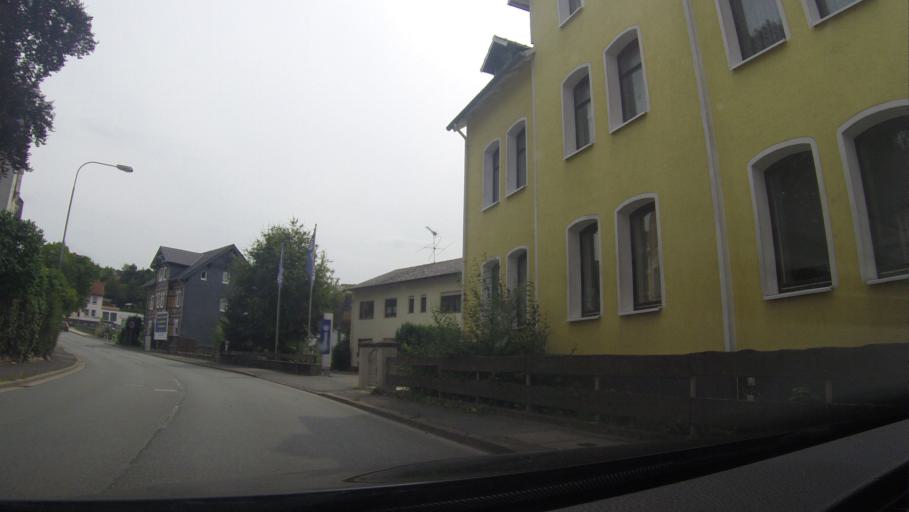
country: DE
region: Hesse
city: Frankenberg
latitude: 51.0623
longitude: 8.7997
